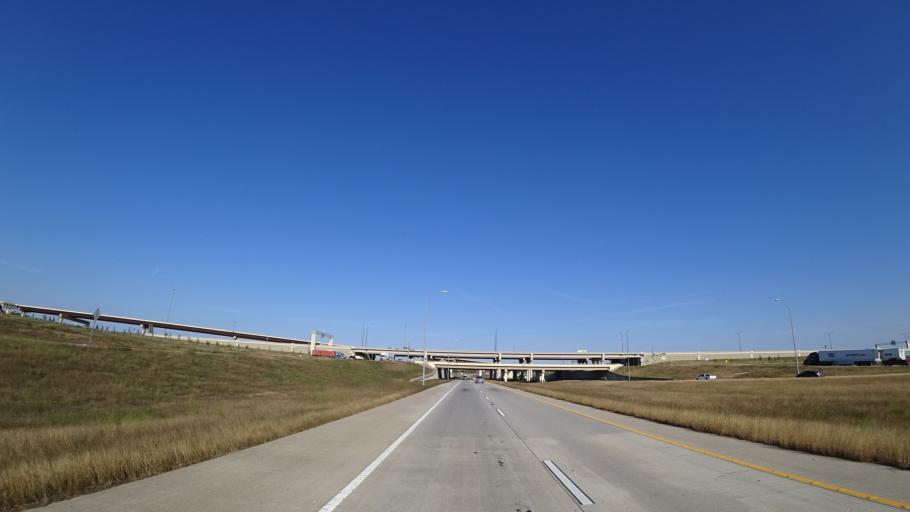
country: US
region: Texas
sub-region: Travis County
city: Manor
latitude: 30.3386
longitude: -97.5905
